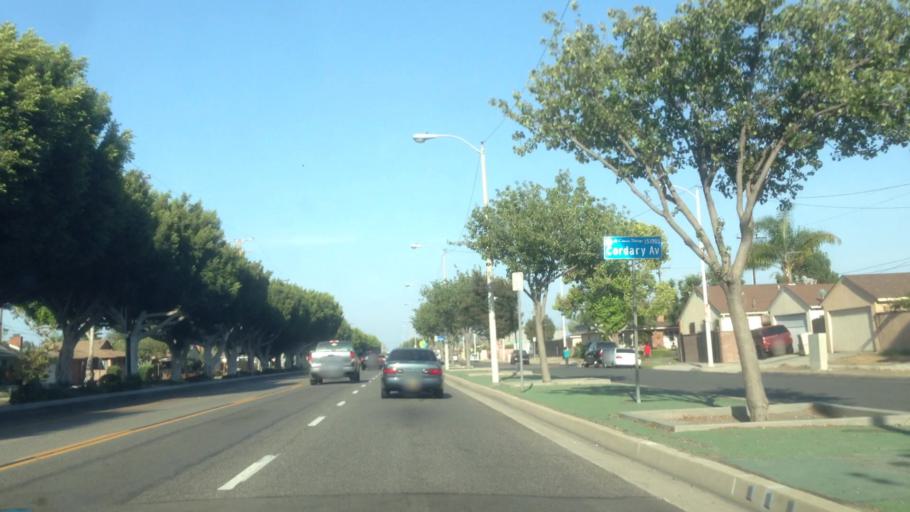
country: US
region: California
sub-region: Los Angeles County
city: Alondra Park
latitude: 33.8946
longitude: -118.3411
